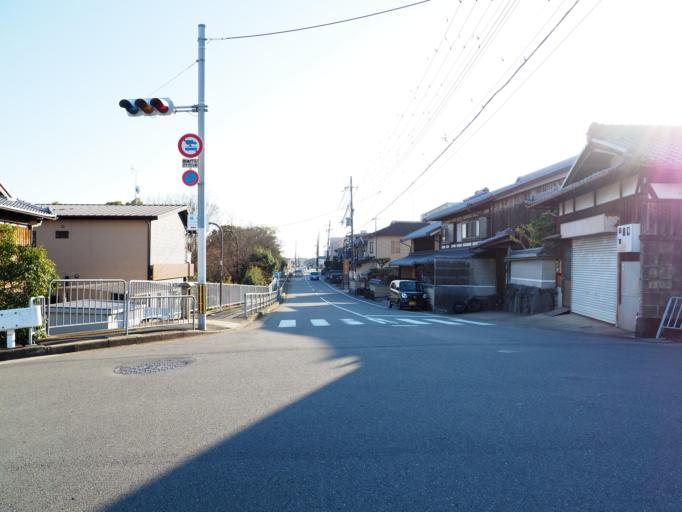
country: JP
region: Kyoto
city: Muko
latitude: 34.9506
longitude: 135.7432
